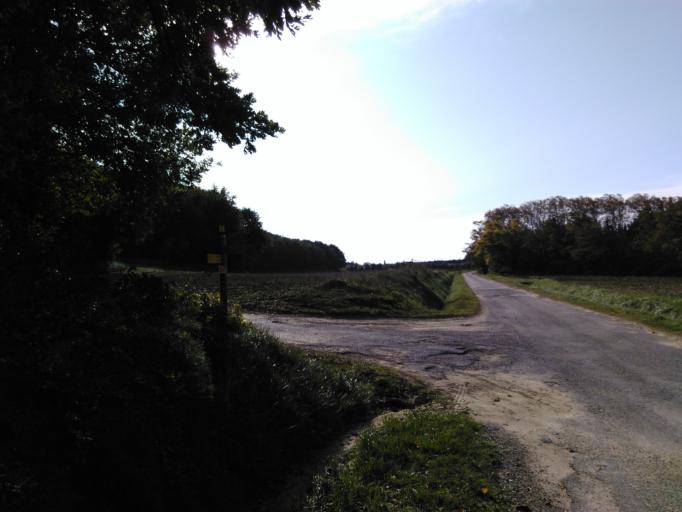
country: FR
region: Provence-Alpes-Cote d'Azur
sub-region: Departement du Vaucluse
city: Grillon
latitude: 44.4042
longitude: 4.9400
